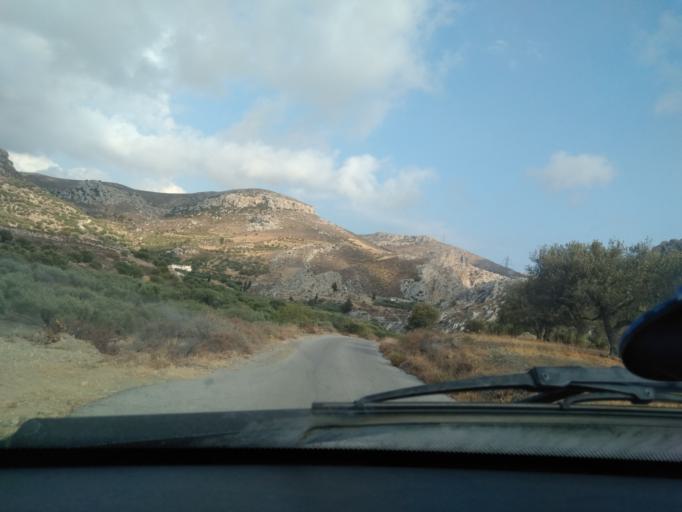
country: GR
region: Crete
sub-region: Nomos Lasithiou
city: Makry-Gialos
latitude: 35.0461
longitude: 26.0533
